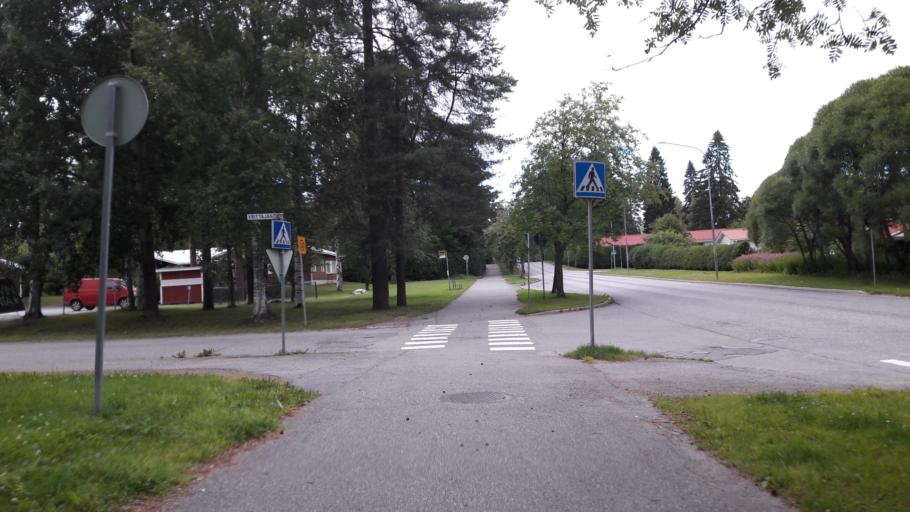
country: FI
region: North Karelia
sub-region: Joensuu
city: Joensuu
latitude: 62.5810
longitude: 29.8048
